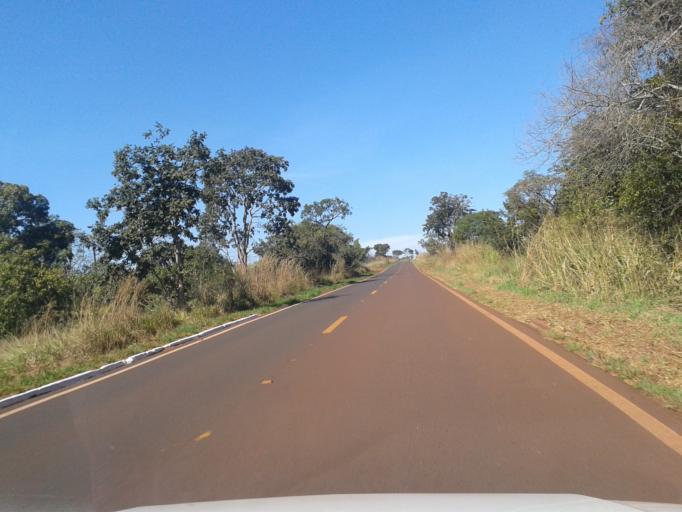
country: BR
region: Minas Gerais
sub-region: Ituiutaba
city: Ituiutaba
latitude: -19.0846
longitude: -49.7656
